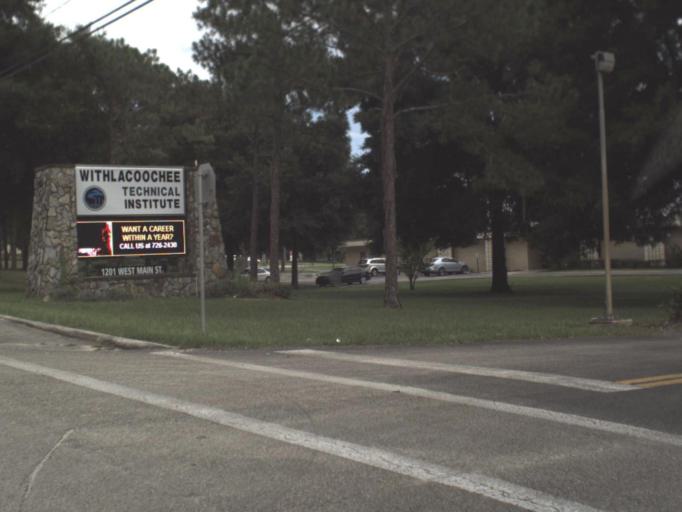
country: US
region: Florida
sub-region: Citrus County
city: Inverness
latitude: 28.8359
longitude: -82.3462
